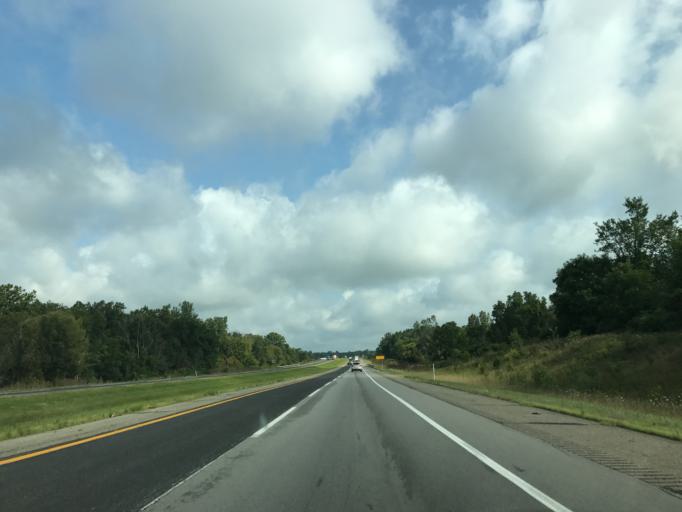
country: US
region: Indiana
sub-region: Steuben County
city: Fremont
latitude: 41.6502
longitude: -84.8430
